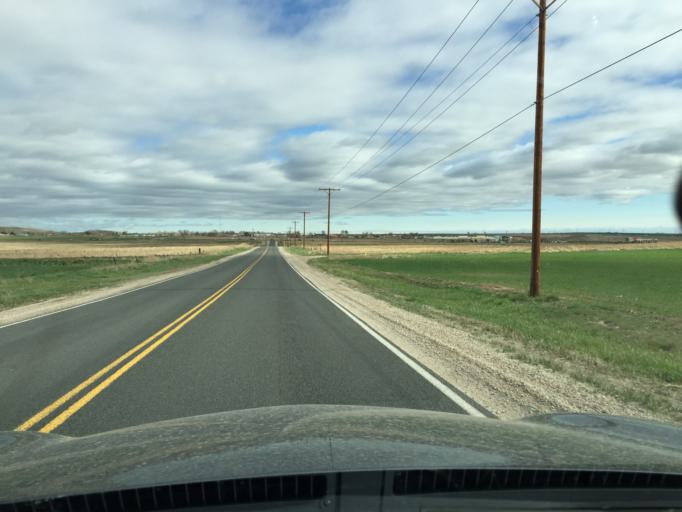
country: US
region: Colorado
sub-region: Boulder County
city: Erie
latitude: 39.9927
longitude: -104.9973
